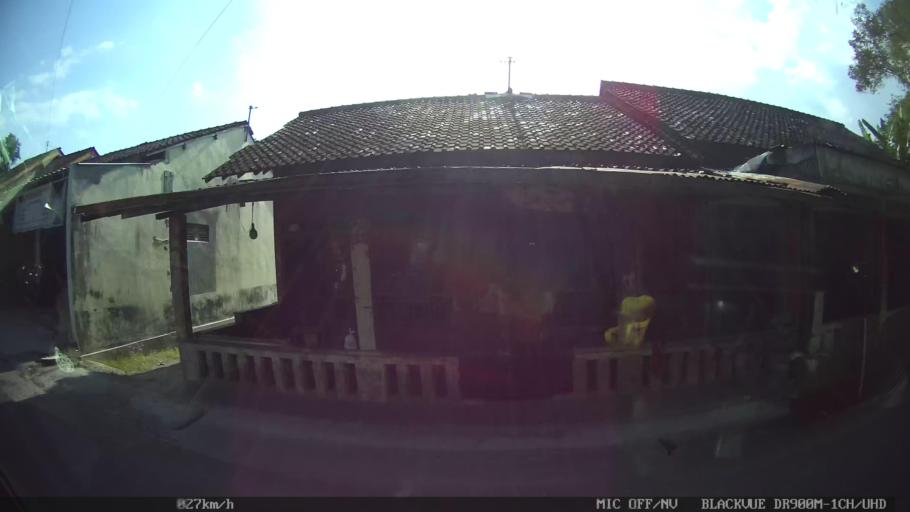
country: ID
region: Daerah Istimewa Yogyakarta
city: Kasihan
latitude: -7.8326
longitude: 110.3386
